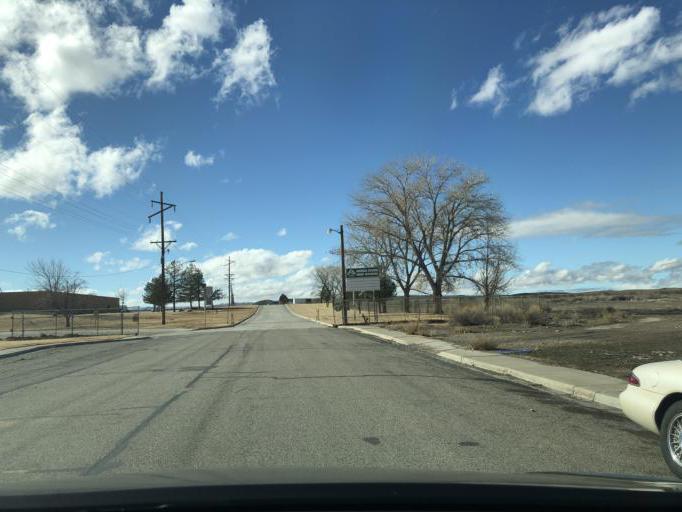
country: US
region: Utah
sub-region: Carbon County
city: East Carbon City
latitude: 39.0007
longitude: -110.1711
